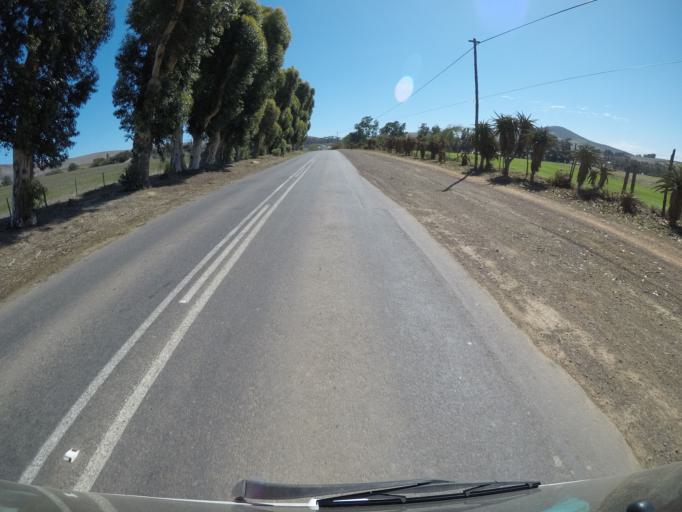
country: ZA
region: Western Cape
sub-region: City of Cape Town
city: Kraaifontein
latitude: -33.8119
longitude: 18.6289
